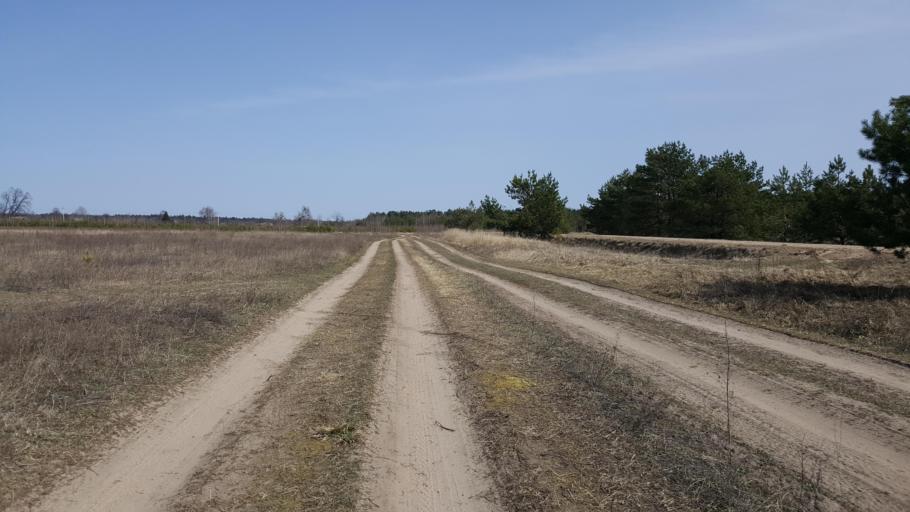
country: BY
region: Brest
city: Kamyanyuki
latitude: 52.5634
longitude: 23.7673
